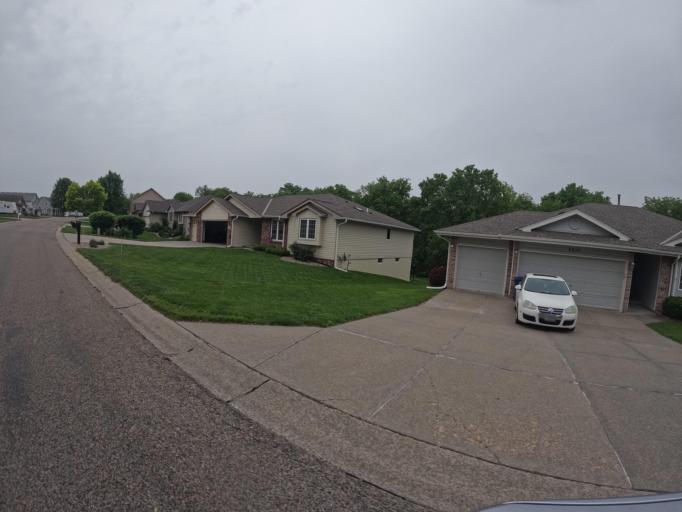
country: US
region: Nebraska
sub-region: Sarpy County
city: Offutt Air Force Base
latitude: 41.0478
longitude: -95.9745
